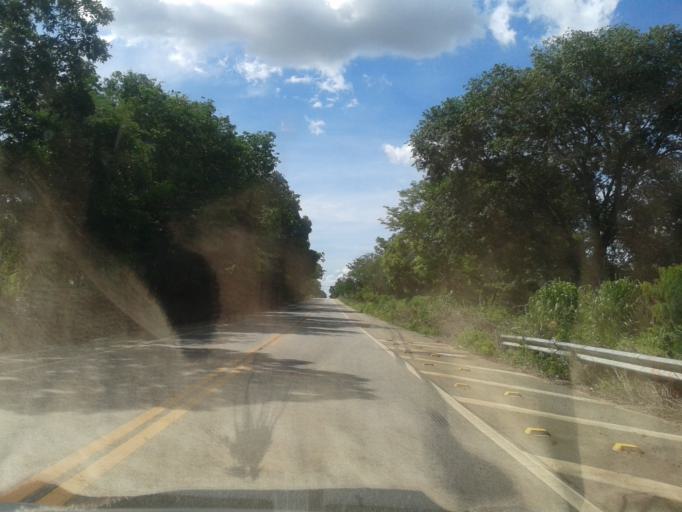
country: BR
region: Goias
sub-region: Itapuranga
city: Itapuranga
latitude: -15.4833
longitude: -50.3296
